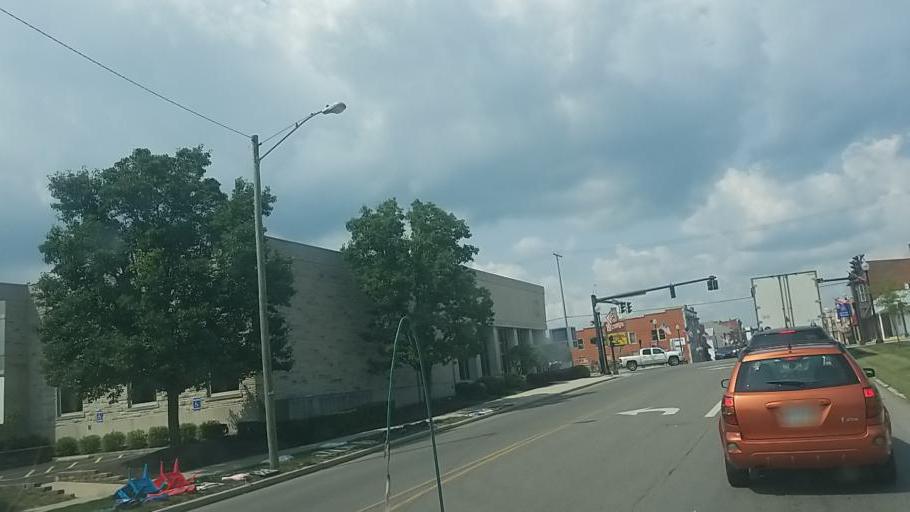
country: US
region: Ohio
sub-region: Crawford County
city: Bucyrus
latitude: 40.8048
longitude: -82.9755
